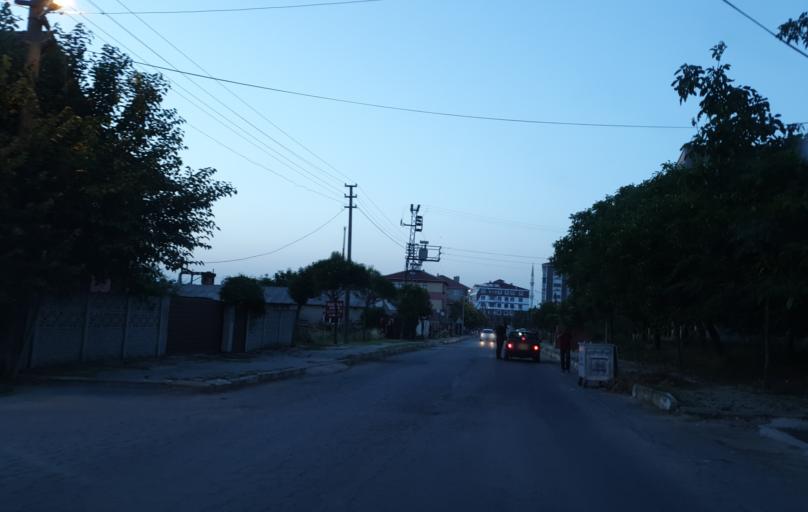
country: TR
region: Tekirdag
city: Saray
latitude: 41.3705
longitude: 27.9300
